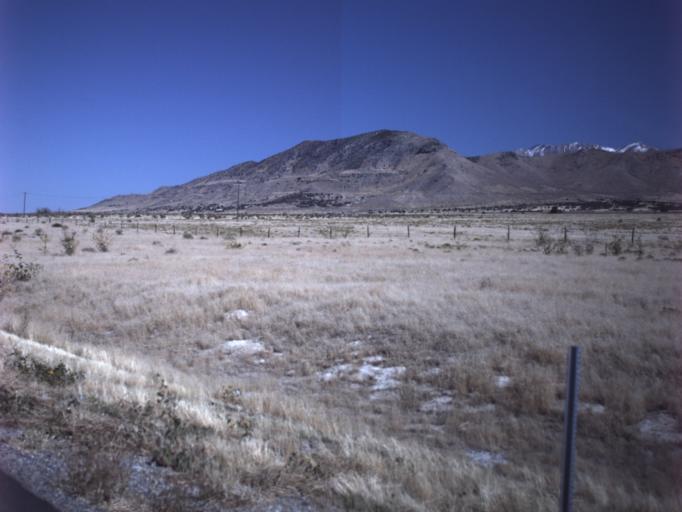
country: US
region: Utah
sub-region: Tooele County
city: Grantsville
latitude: 40.5168
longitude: -112.7477
